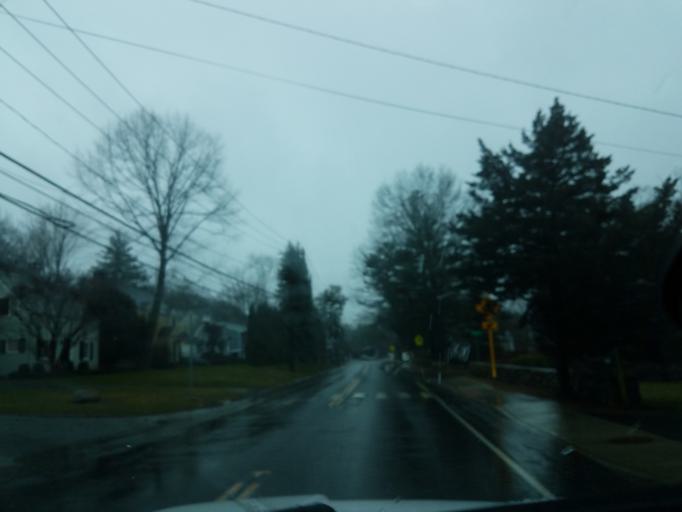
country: US
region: Connecticut
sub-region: Fairfield County
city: Stamford
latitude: 41.0843
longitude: -73.5119
